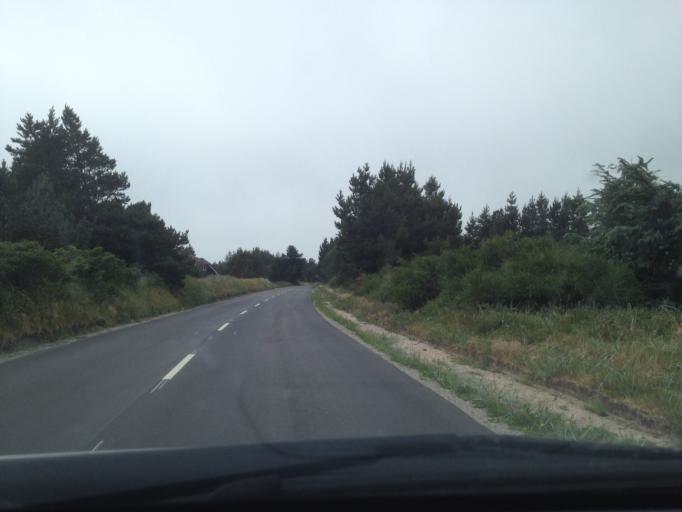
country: DK
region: South Denmark
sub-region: Varde Kommune
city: Oksbol
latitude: 55.5531
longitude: 8.1606
